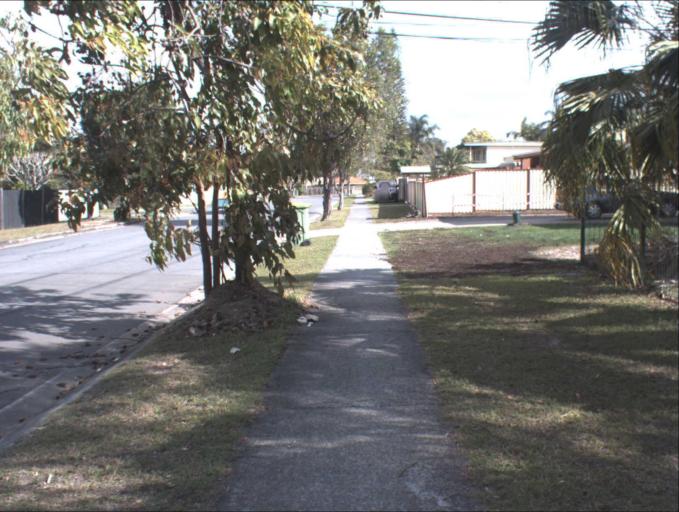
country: AU
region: Queensland
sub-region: Logan
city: Waterford West
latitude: -27.6737
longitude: 153.1324
